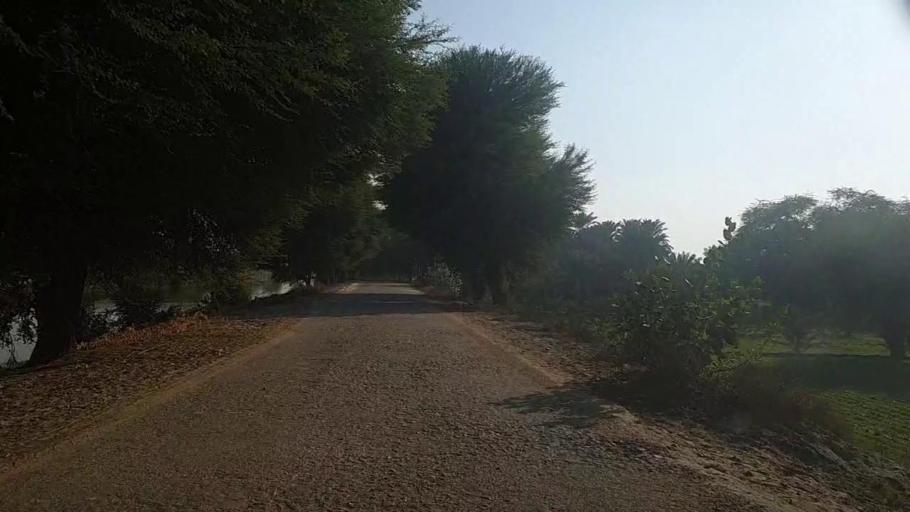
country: PK
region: Sindh
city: Bozdar
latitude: 27.2556
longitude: 68.6765
